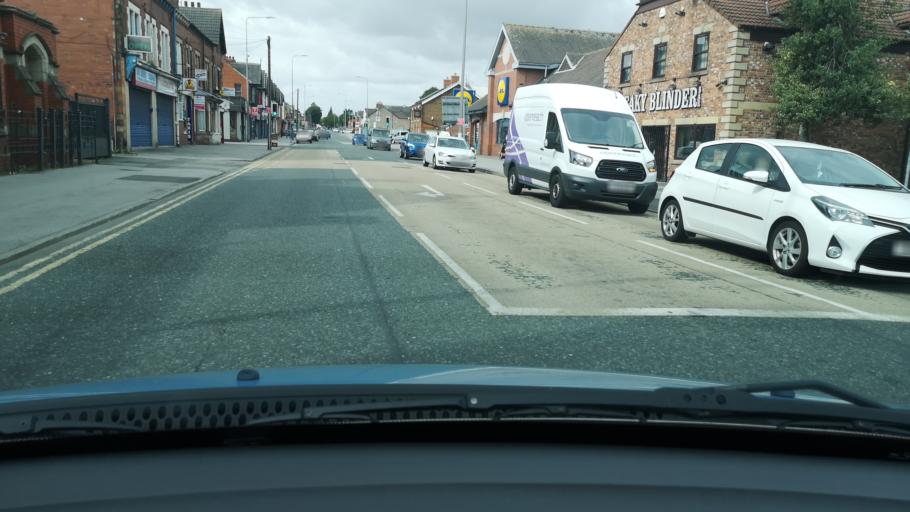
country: GB
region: England
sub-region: North Lincolnshire
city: Scunthorpe
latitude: 53.5910
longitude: -0.6542
